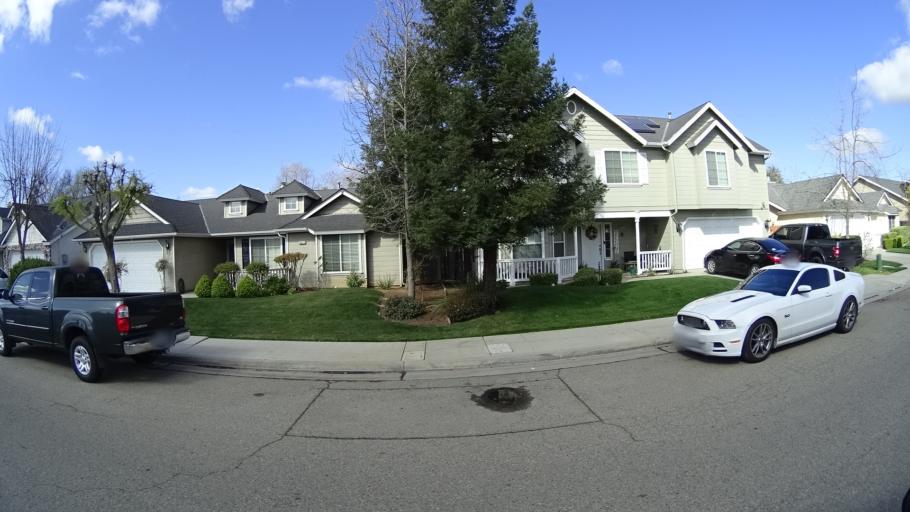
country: US
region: California
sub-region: Fresno County
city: West Park
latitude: 36.8343
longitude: -119.8879
